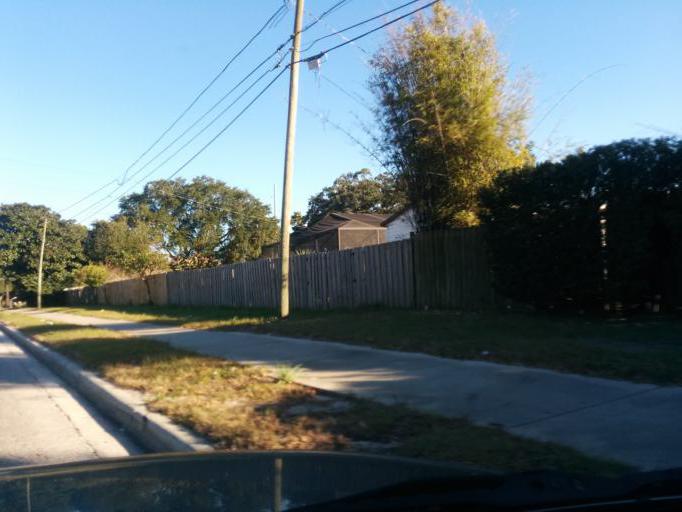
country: US
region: Florida
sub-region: Pinellas County
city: Kenneth City
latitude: 27.8063
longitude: -82.7052
